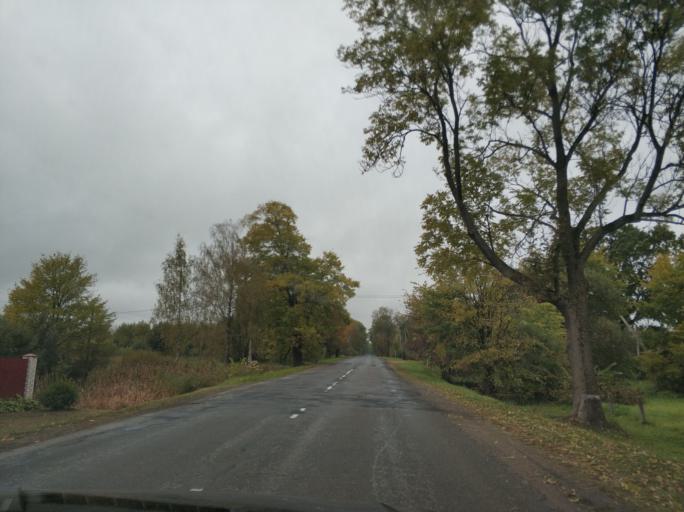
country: BY
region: Vitebsk
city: Polatsk
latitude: 55.4303
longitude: 28.9975
